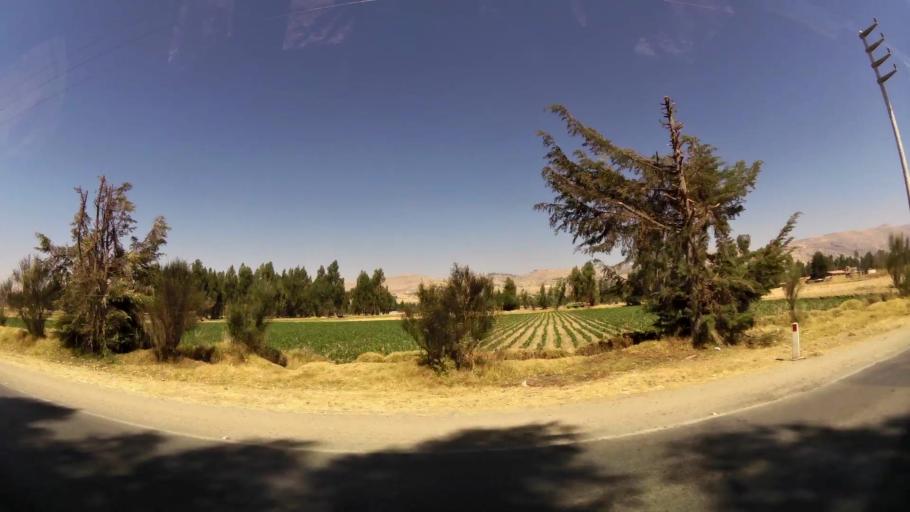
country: PE
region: Junin
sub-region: Provincia de Concepcion
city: Matahuasi
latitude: -11.8768
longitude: -75.3617
